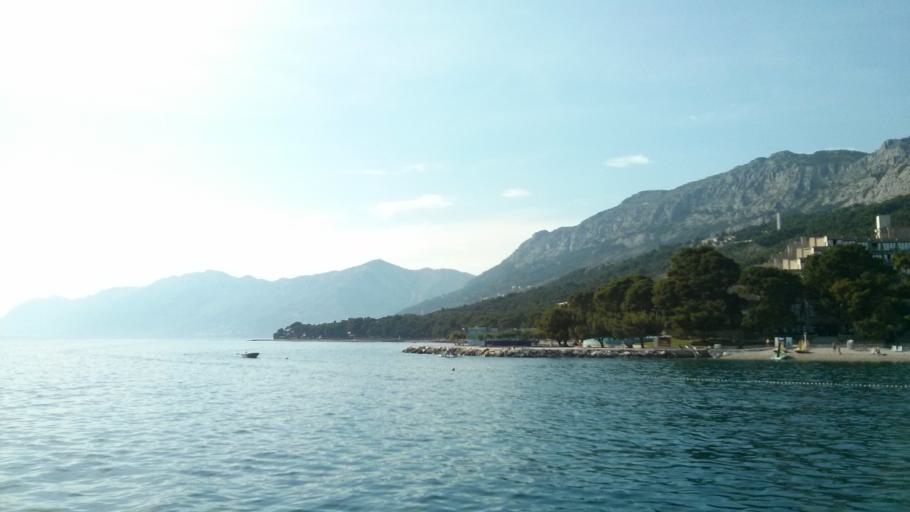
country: HR
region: Splitsko-Dalmatinska
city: Donja Brela
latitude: 43.3658
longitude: 16.9301
